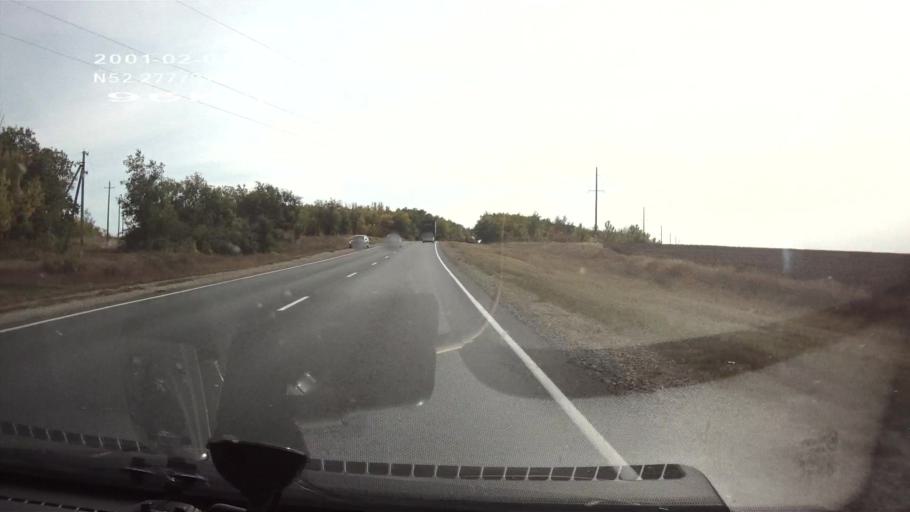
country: RU
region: Saratov
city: Alekseyevka
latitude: 52.2773
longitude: 47.9326
